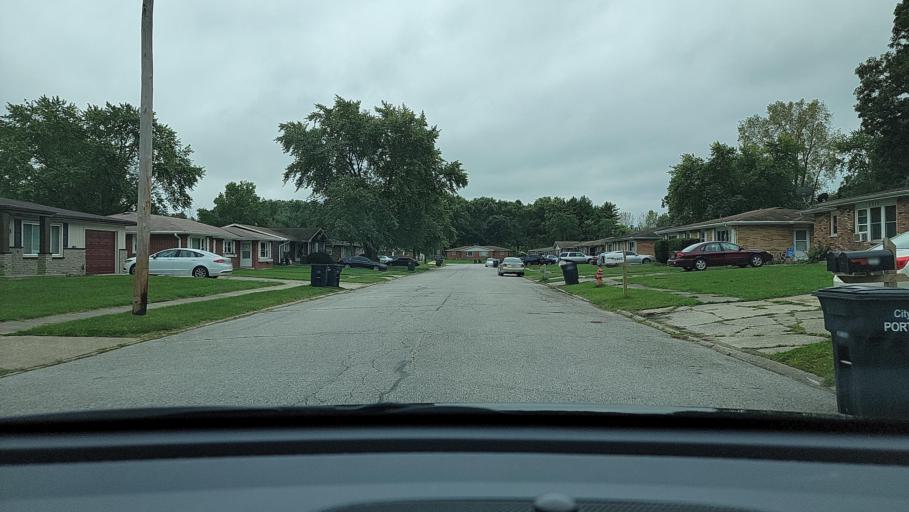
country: US
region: Indiana
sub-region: Porter County
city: Portage
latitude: 41.5561
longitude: -87.2064
